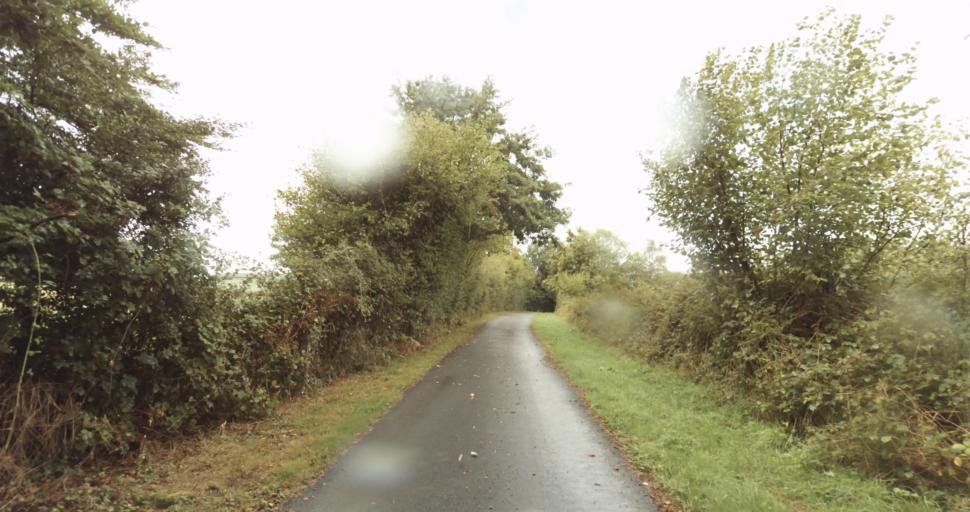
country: FR
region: Lower Normandy
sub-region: Departement de l'Orne
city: Sainte-Gauburge-Sainte-Colombe
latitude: 48.6967
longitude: 0.4133
